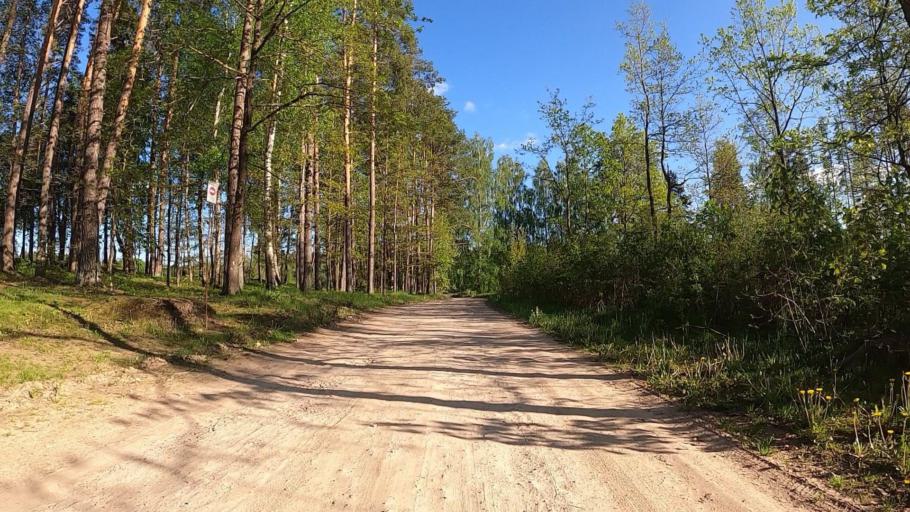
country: LV
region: Baldone
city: Baldone
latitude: 56.7712
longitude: 24.3349
